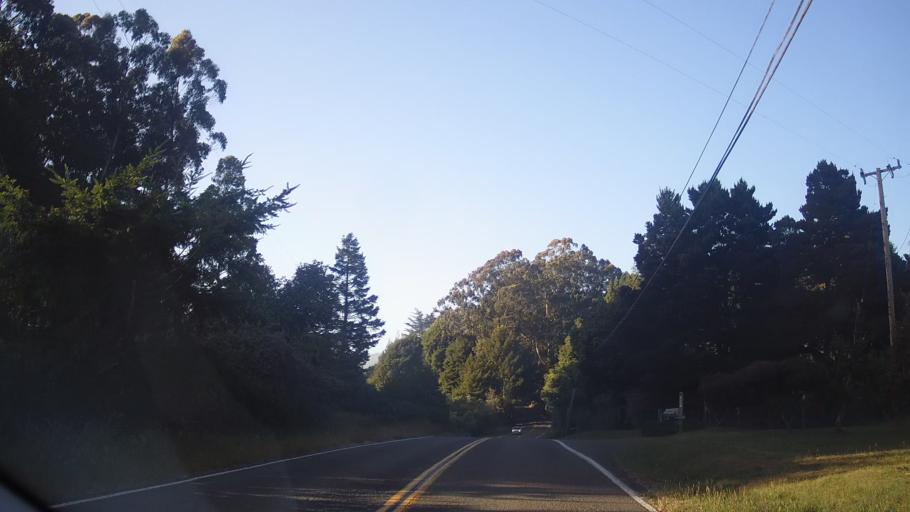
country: US
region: California
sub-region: Mendocino County
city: Fort Bragg
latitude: 39.5208
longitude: -123.7615
